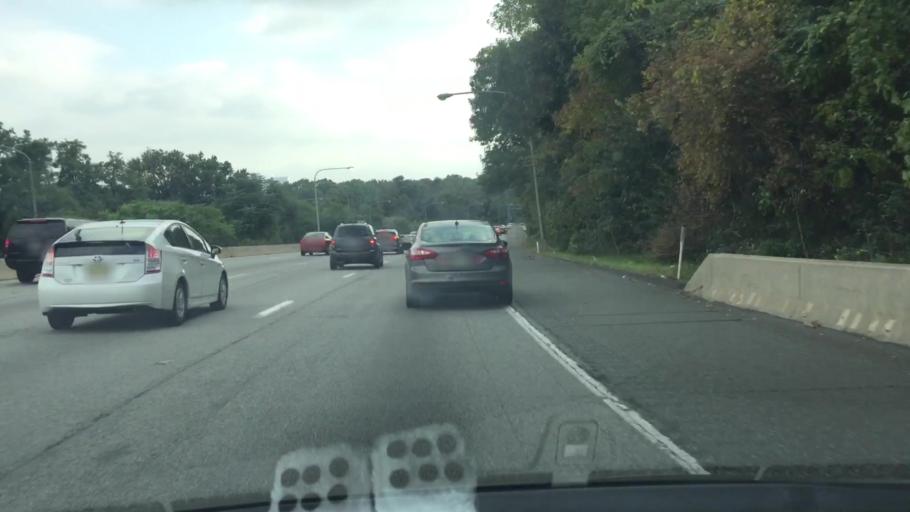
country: US
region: Pennsylvania
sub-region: Montgomery County
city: Bala-Cynwyd
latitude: 40.0022
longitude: -75.1950
